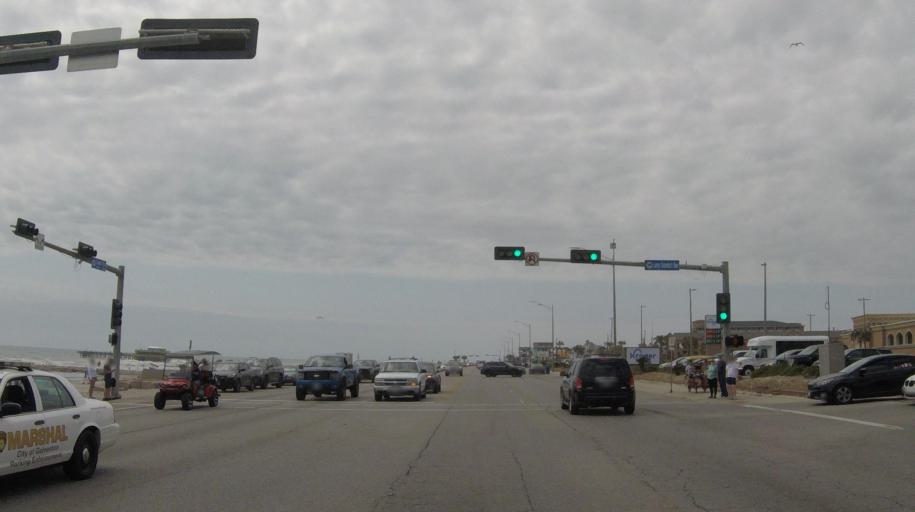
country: US
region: Texas
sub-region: Galveston County
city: Galveston
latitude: 29.2689
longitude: -94.8223
